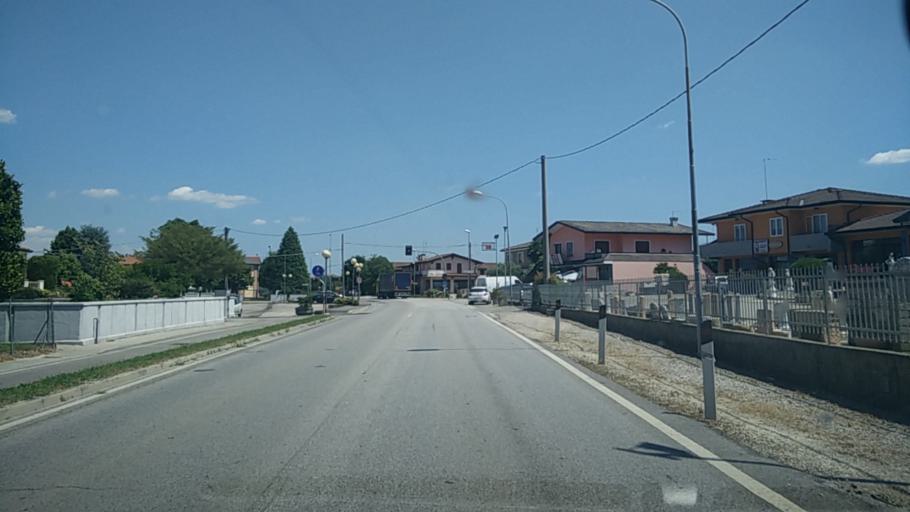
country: IT
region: Veneto
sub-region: Provincia di Padova
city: Tombolo
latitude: 45.6190
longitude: 11.8026
